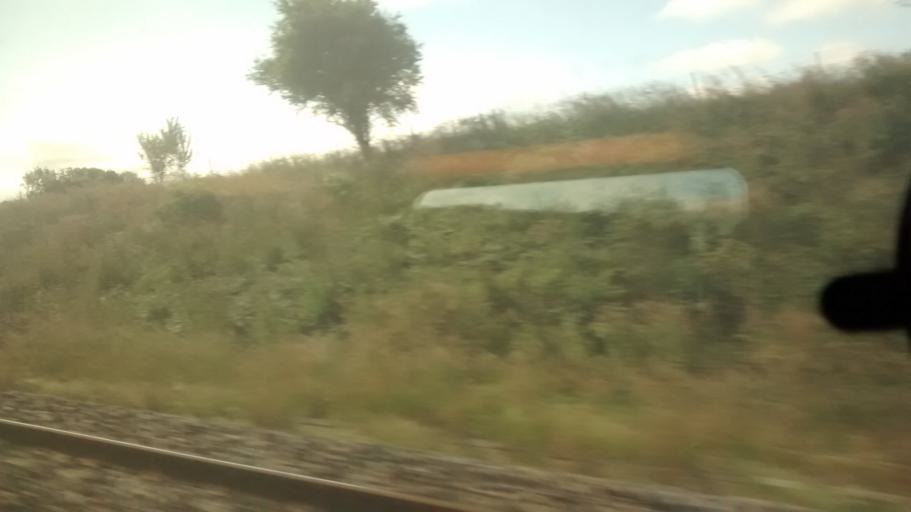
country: FR
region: Centre
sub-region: Departement d'Eure-et-Loir
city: La Bazoche-Gouet
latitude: 48.0855
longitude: 0.8998
